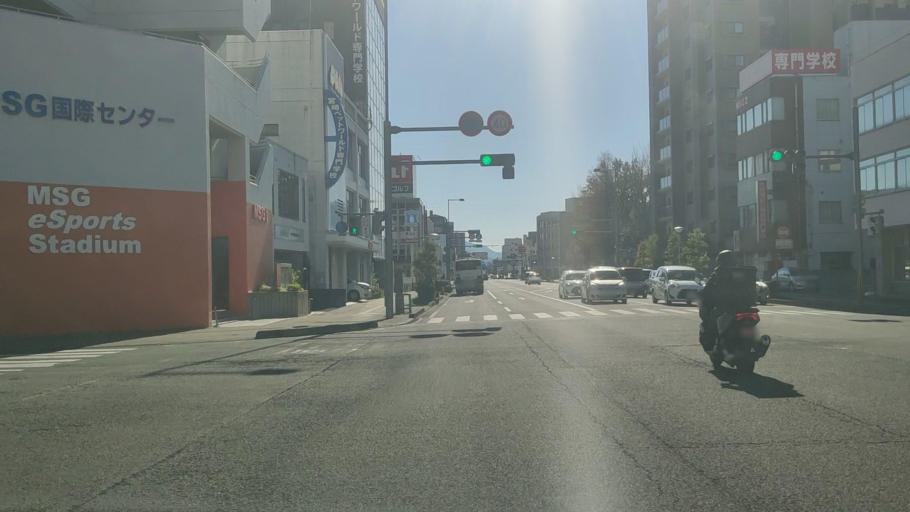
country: JP
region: Miyazaki
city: Miyazaki-shi
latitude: 31.9129
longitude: 131.4300
